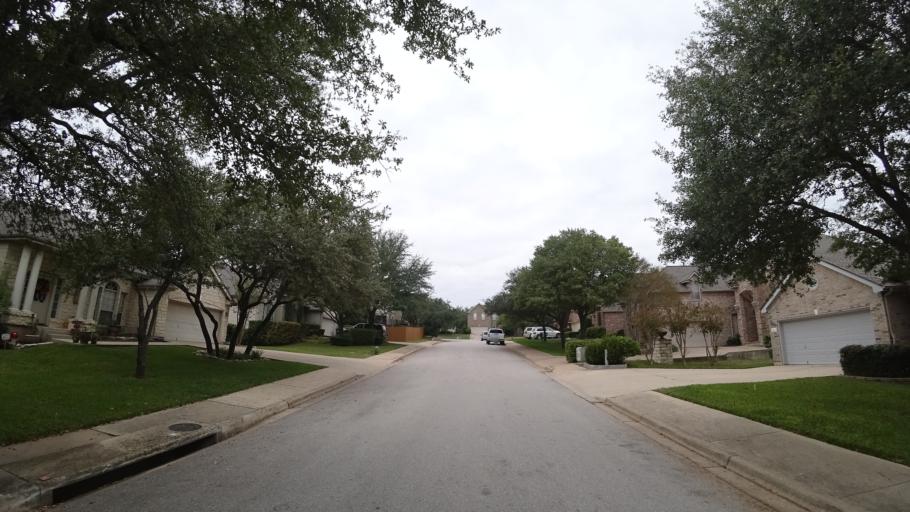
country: US
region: Texas
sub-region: Travis County
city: Bee Cave
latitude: 30.3106
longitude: -97.9220
